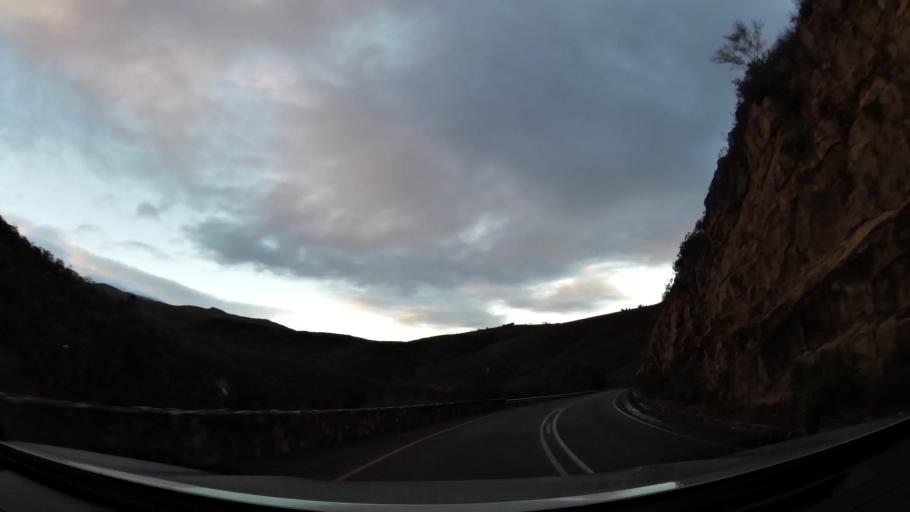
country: ZA
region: Western Cape
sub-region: Overberg District Municipality
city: Swellendam
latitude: -33.9889
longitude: 20.7122
